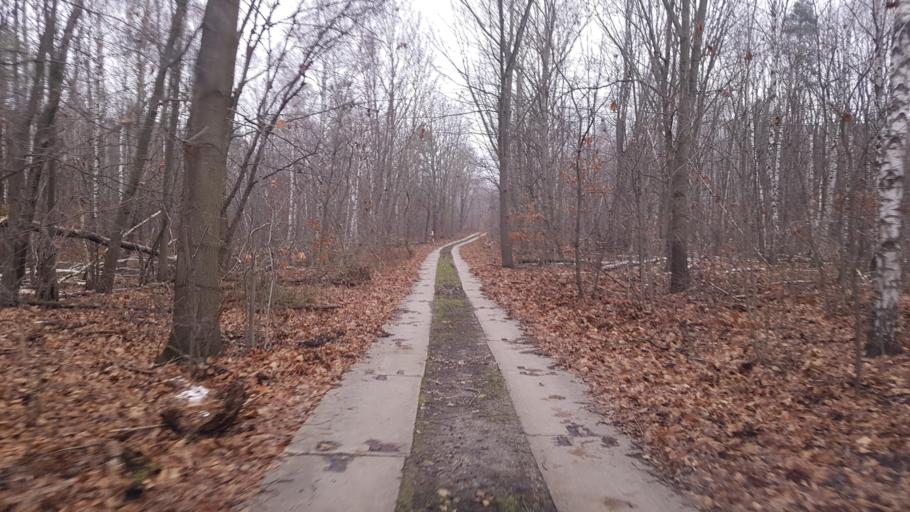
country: DE
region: Brandenburg
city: Plessa
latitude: 51.4935
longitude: 13.6374
